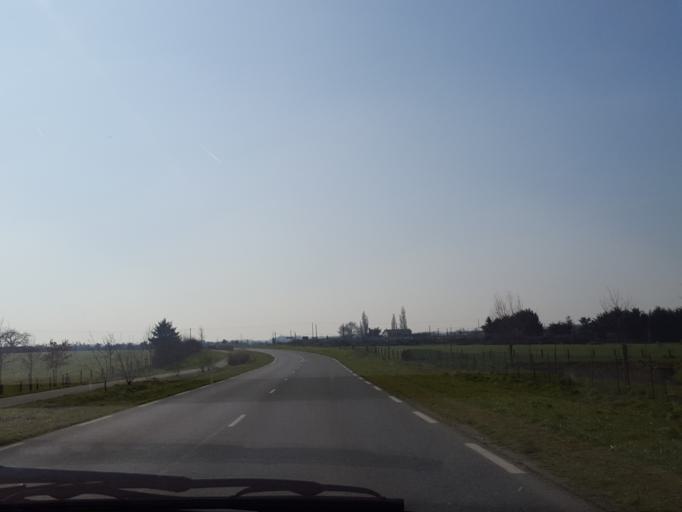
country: FR
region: Pays de la Loire
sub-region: Departement de la Vendee
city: Saint-Fulgent
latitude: 46.8586
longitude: -1.1891
